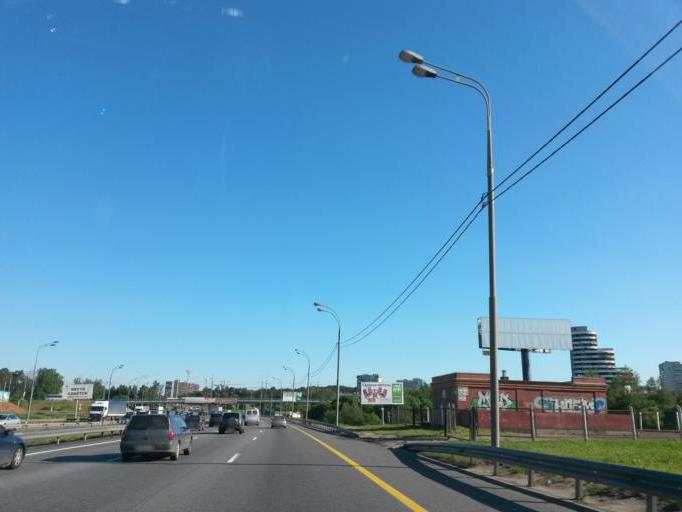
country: RU
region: Moskovskaya
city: Vidnoye
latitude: 55.5412
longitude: 37.6972
